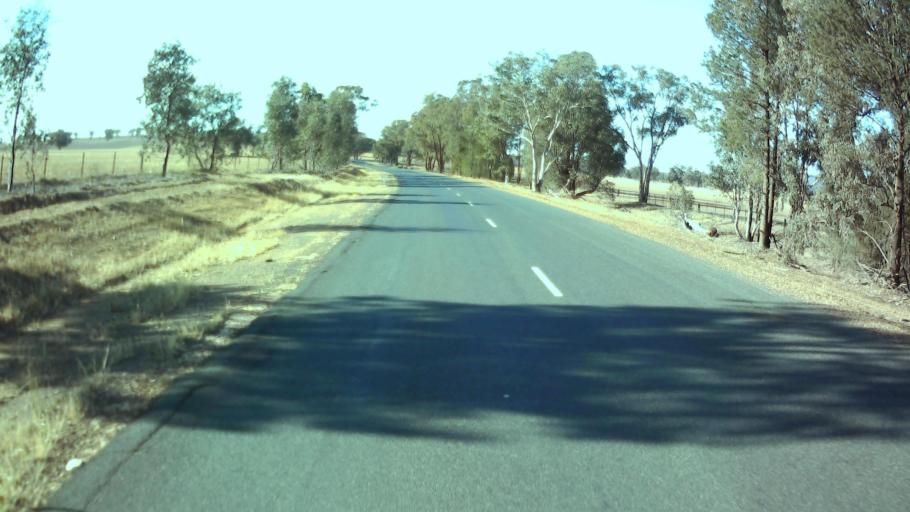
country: AU
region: New South Wales
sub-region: Weddin
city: Grenfell
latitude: -33.9306
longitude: 148.1374
